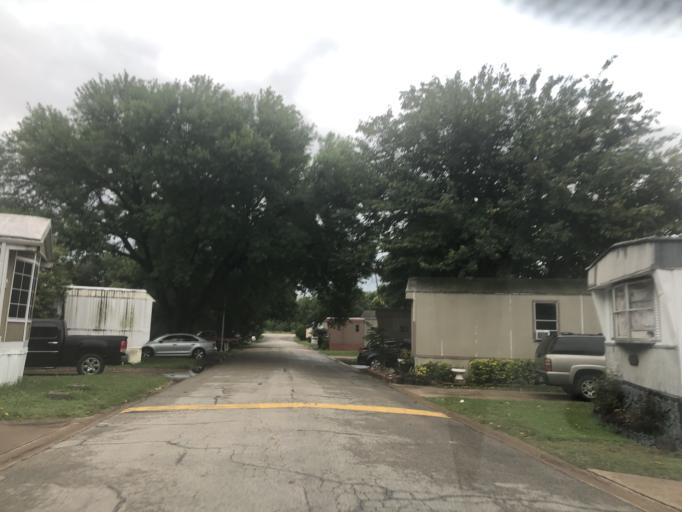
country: US
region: Texas
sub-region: Dallas County
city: Irving
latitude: 32.7846
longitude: -96.9718
